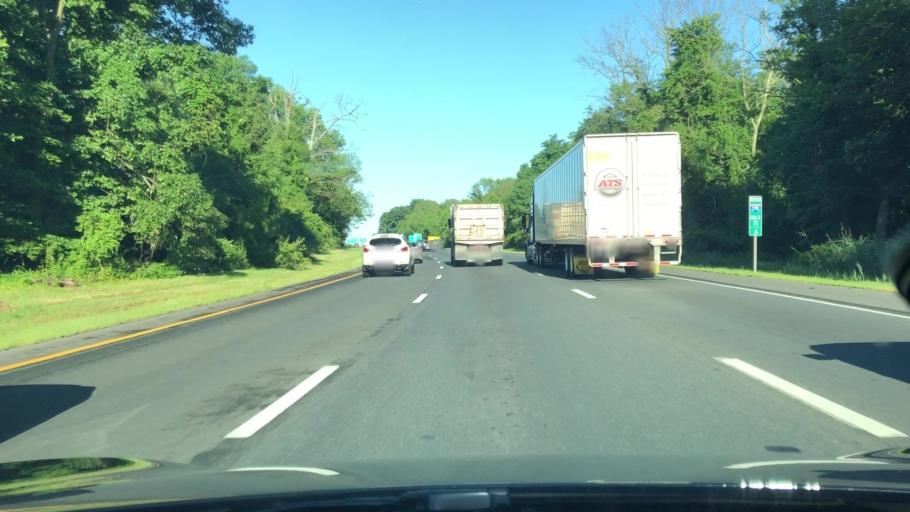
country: US
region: New Jersey
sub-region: Mercer County
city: Ewing
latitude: 40.2929
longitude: -74.7720
